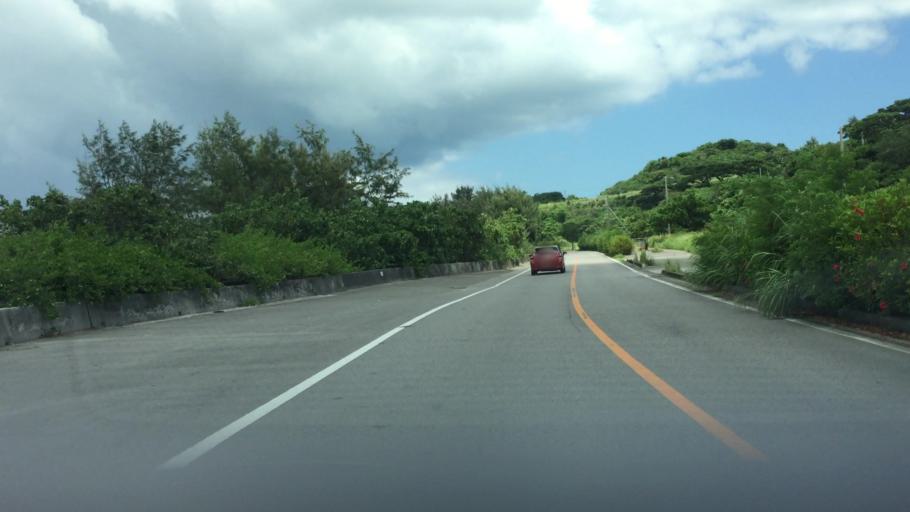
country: JP
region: Okinawa
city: Ishigaki
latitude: 24.4240
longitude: 124.1294
